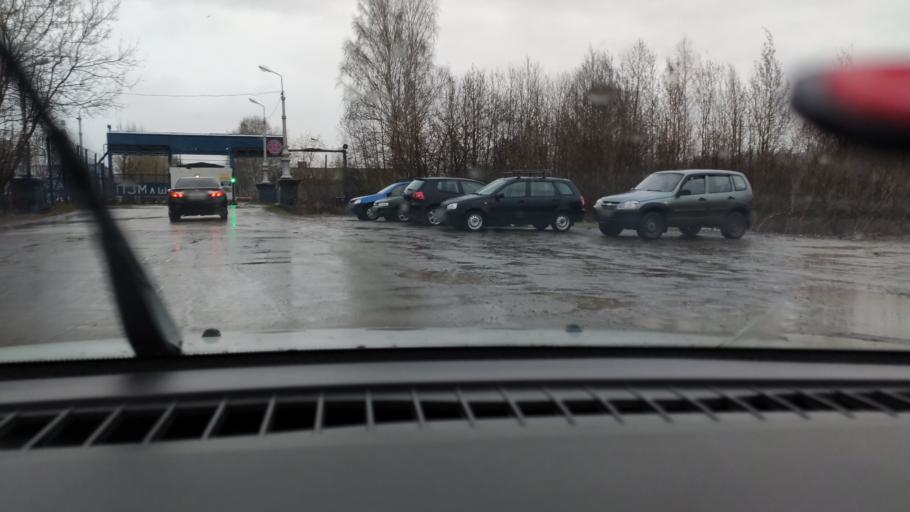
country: RU
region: Perm
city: Perm
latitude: 58.0594
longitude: 56.3271
